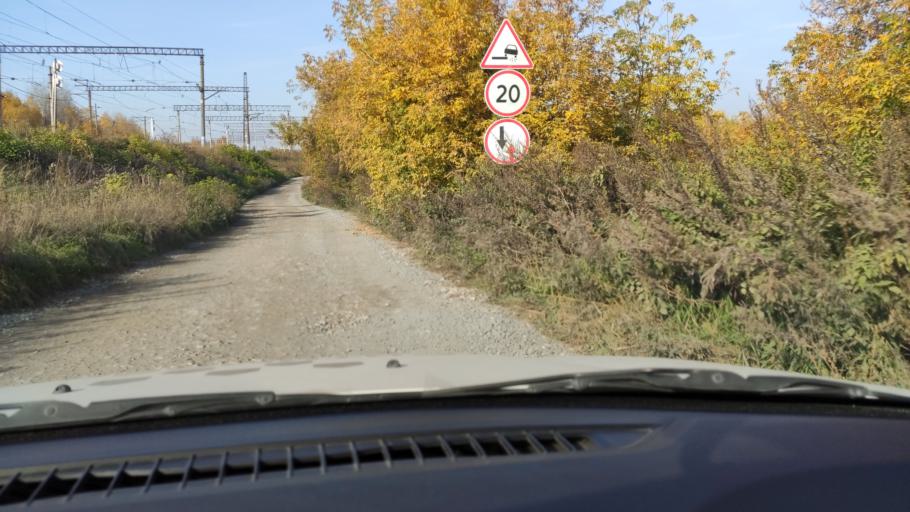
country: RU
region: Perm
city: Sylva
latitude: 58.0428
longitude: 56.7480
